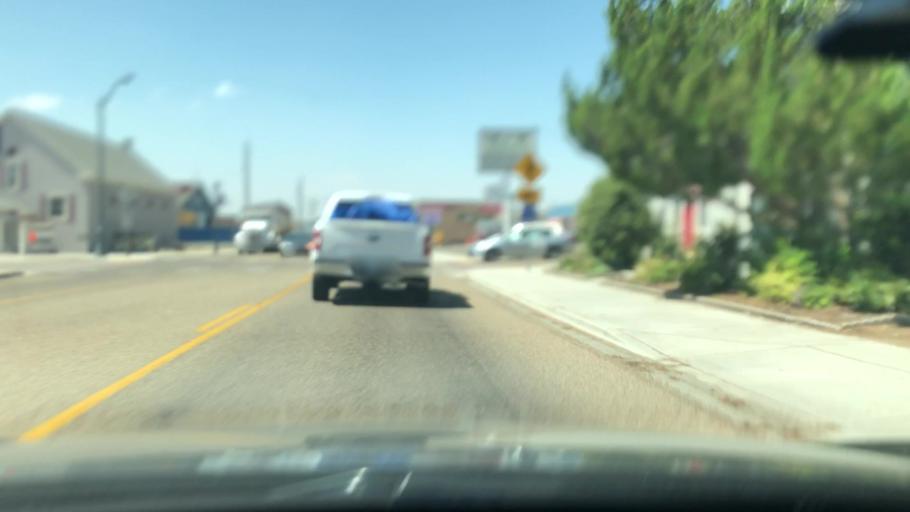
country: US
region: Idaho
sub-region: Canyon County
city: Parma
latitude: 43.7860
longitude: -116.9448
